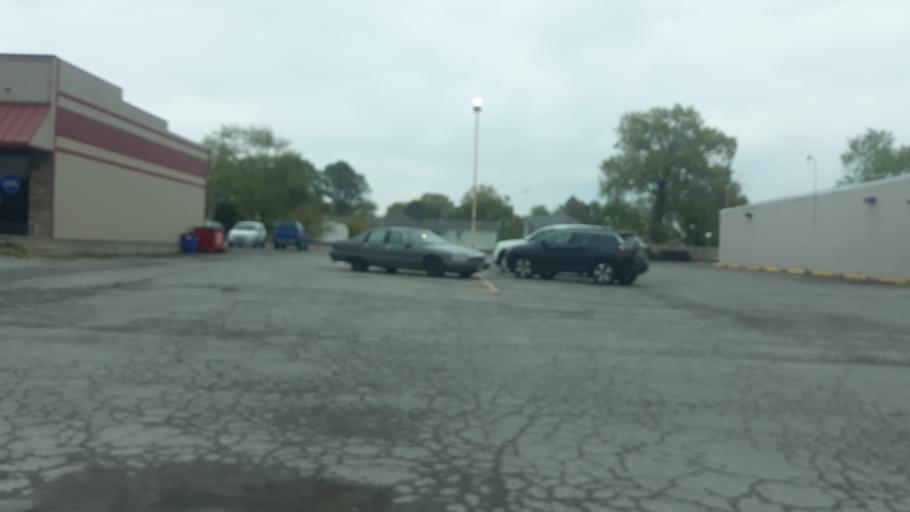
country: US
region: Illinois
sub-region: Williamson County
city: Marion
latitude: 37.7362
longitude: -88.9326
